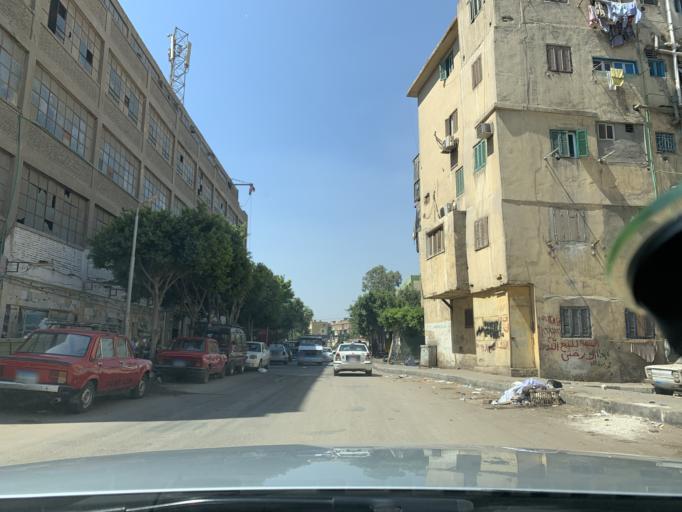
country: EG
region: Muhafazat al Qahirah
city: Cairo
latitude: 30.0735
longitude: 31.2571
